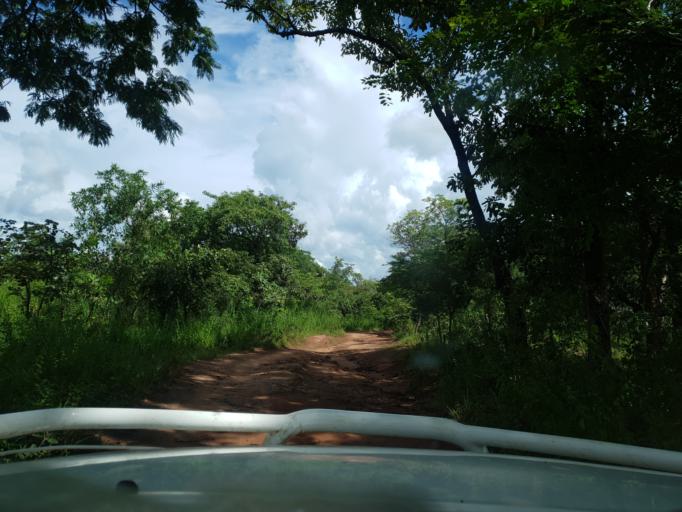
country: CI
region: Savanes
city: Tengrela
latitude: 10.4624
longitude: -6.7968
